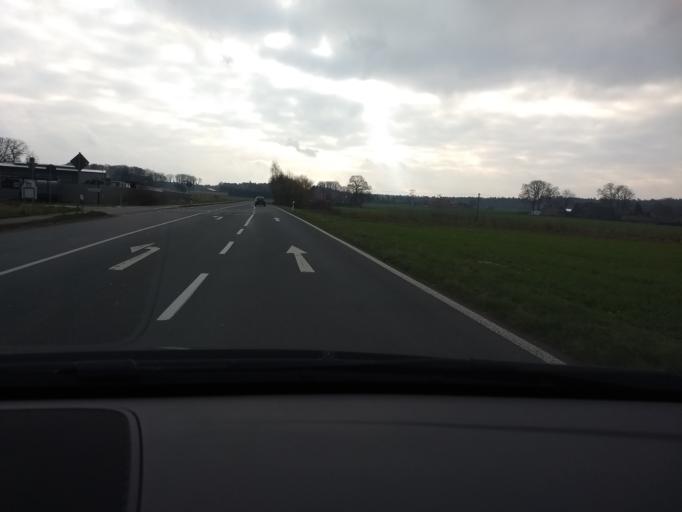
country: DE
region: North Rhine-Westphalia
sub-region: Regierungsbezirk Munster
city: Heiden
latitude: 51.8731
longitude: 6.9172
